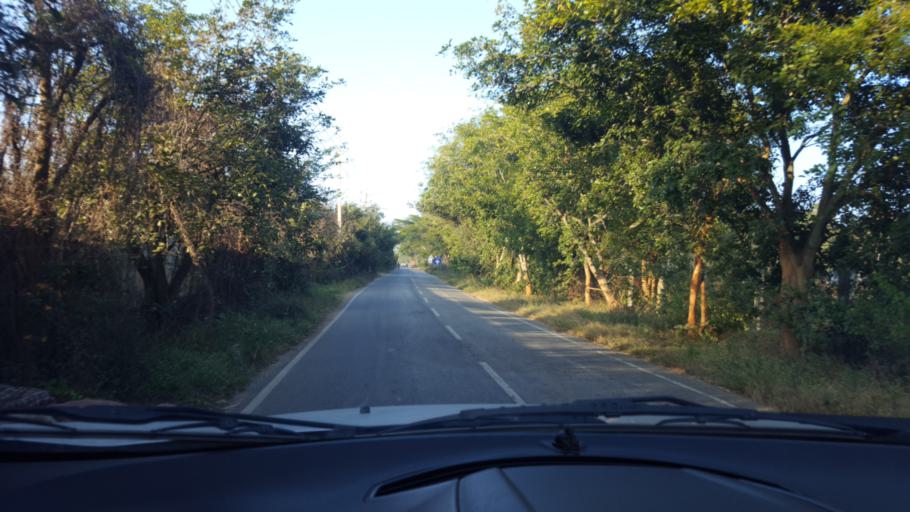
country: IN
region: Karnataka
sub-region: Bangalore Urban
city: Yelahanka
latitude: 13.1768
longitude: 77.5992
